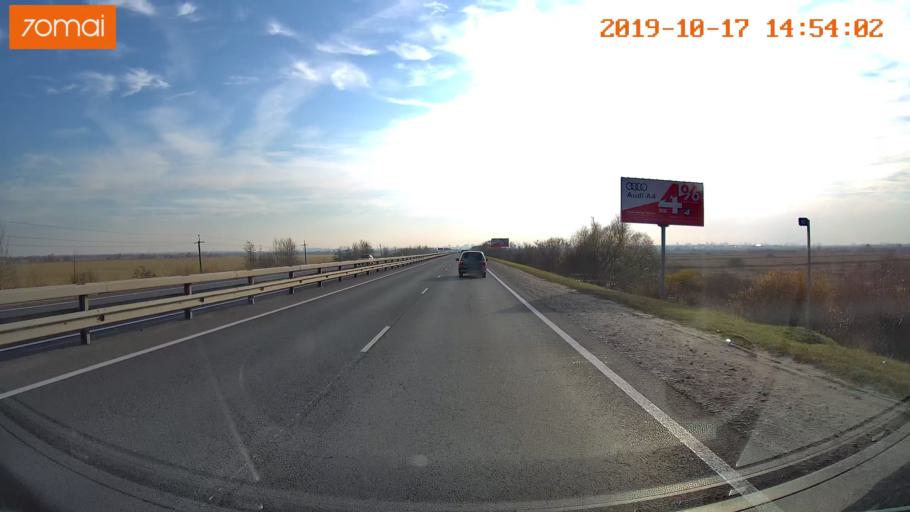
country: RU
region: Rjazan
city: Polyany
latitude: 54.6866
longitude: 39.8347
